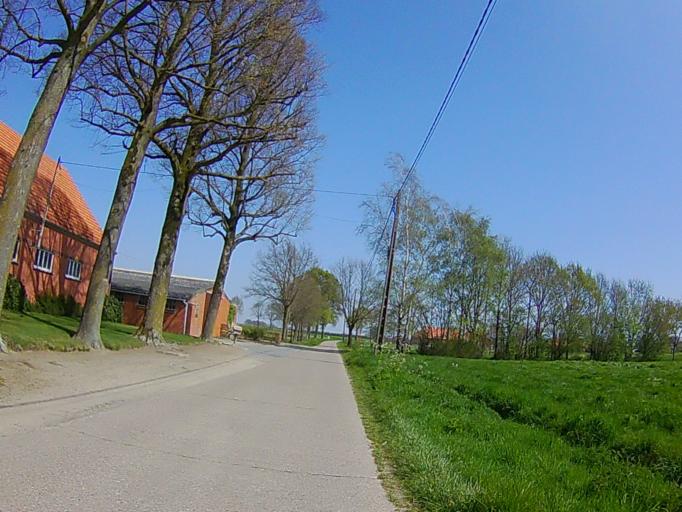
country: BE
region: Flanders
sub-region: Provincie Antwerpen
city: Brecht
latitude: 51.3673
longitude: 4.6887
